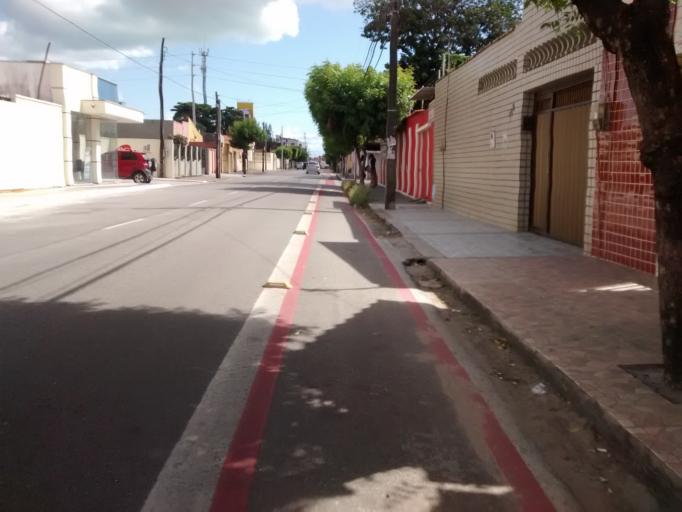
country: BR
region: Ceara
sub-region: Fortaleza
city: Fortaleza
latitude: -3.7371
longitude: -38.5502
